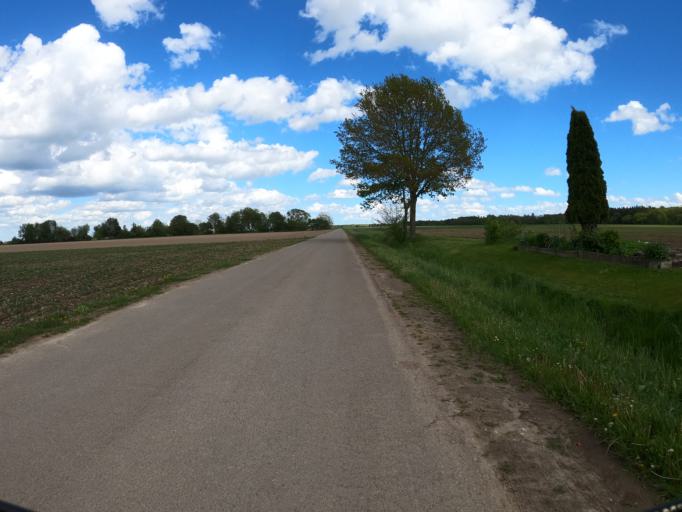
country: DE
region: Bavaria
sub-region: Swabia
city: Leipheim
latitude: 48.4255
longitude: 10.1987
